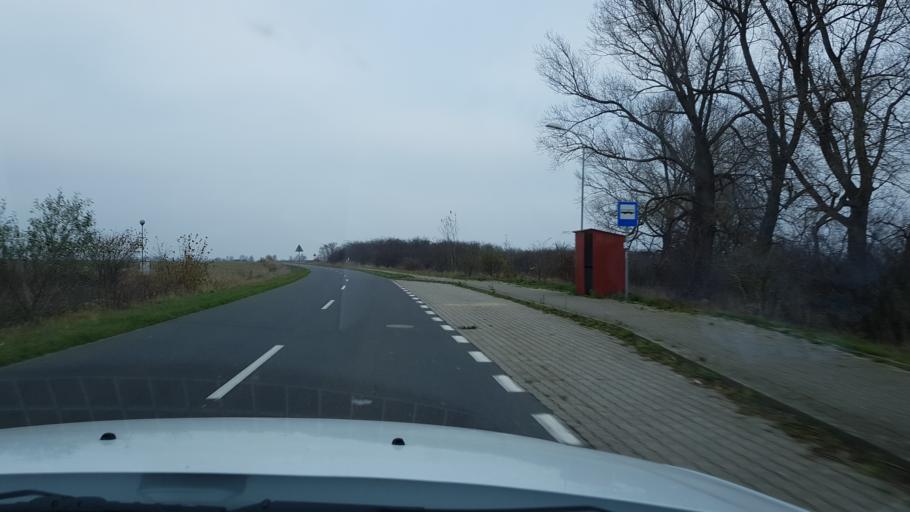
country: PL
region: West Pomeranian Voivodeship
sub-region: Powiat kamienski
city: Kamien Pomorski
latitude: 53.9594
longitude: 14.6858
